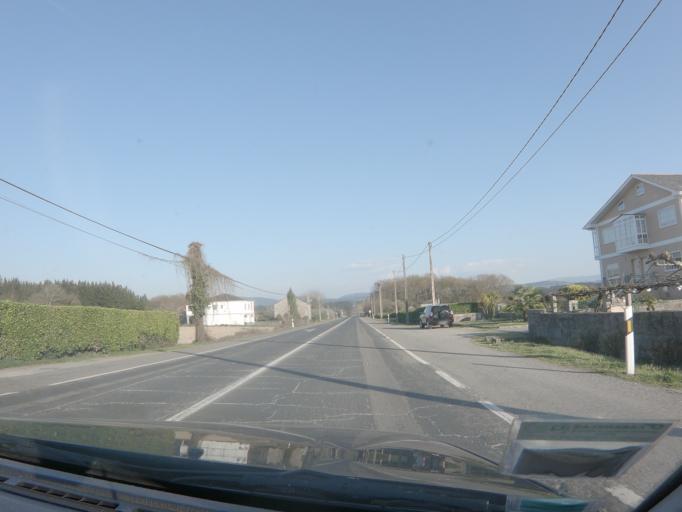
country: ES
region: Galicia
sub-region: Provincia de Lugo
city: Corgo
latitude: 42.9426
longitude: -7.4297
